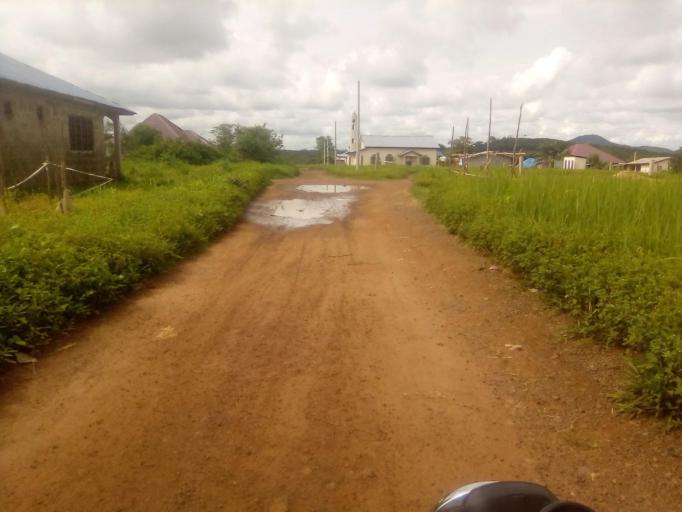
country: SL
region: Southern Province
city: Moyamba
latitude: 8.1490
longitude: -12.4327
